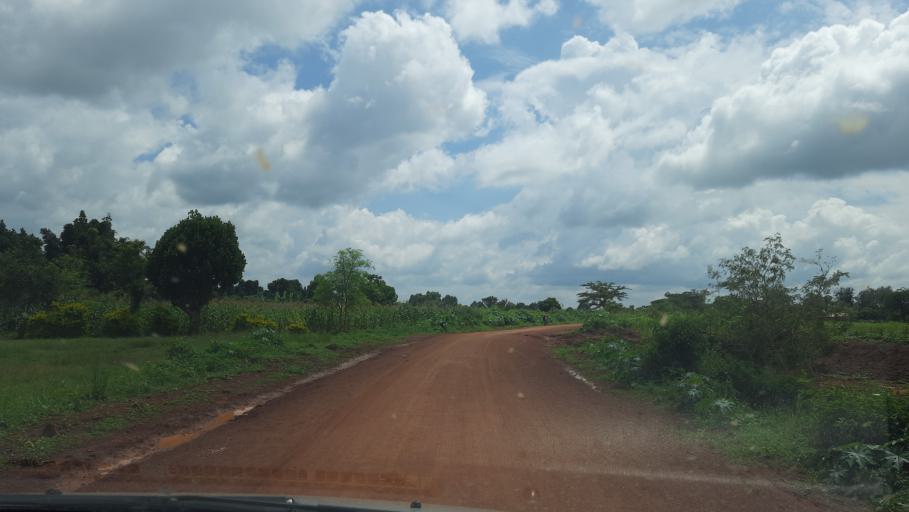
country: UG
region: Western Region
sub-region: Kiryandongo District
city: Kiryandongo
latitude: 1.8245
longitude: 31.9824
